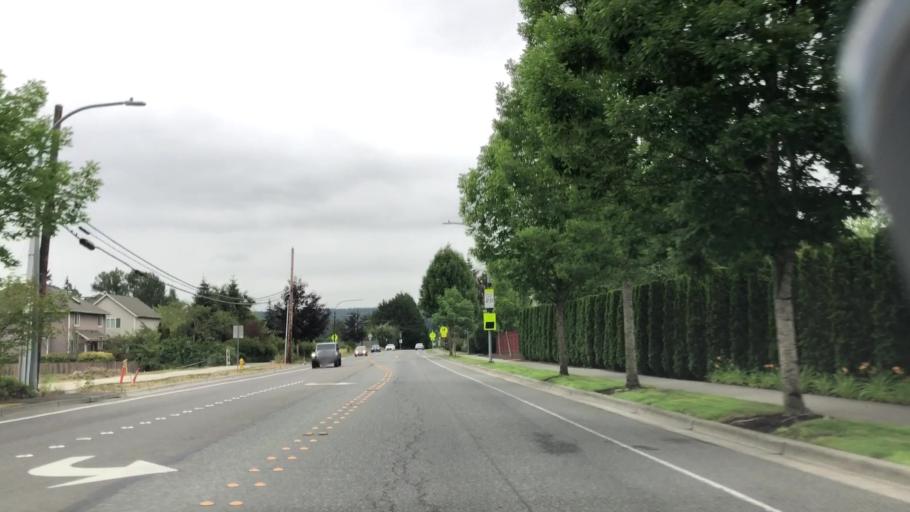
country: US
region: Washington
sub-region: King County
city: Redmond
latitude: 47.7038
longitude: -122.1022
